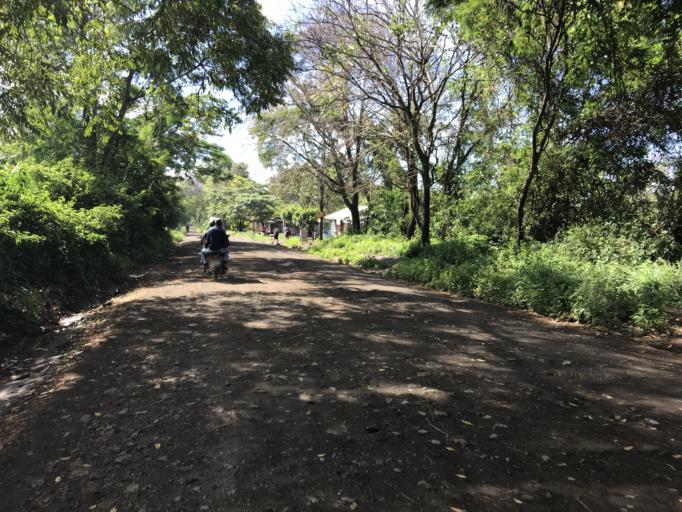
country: TZ
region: Arusha
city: Nkoaranga
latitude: -3.3858
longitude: 36.7965
